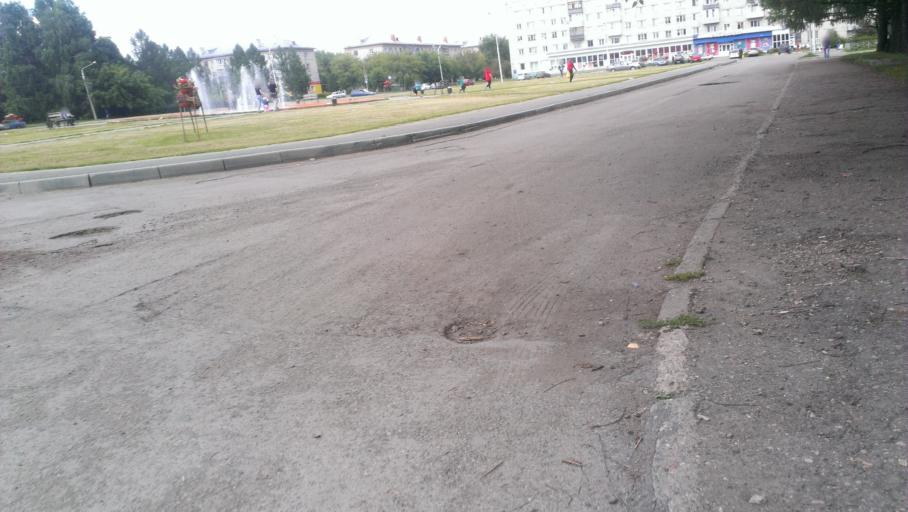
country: RU
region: Altai Krai
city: Yuzhnyy
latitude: 53.2537
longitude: 83.6925
